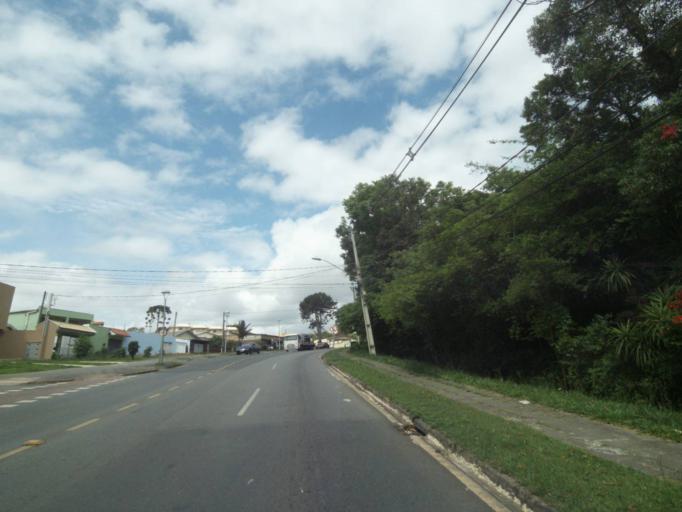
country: BR
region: Parana
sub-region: Curitiba
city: Curitiba
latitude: -25.3845
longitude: -49.2969
